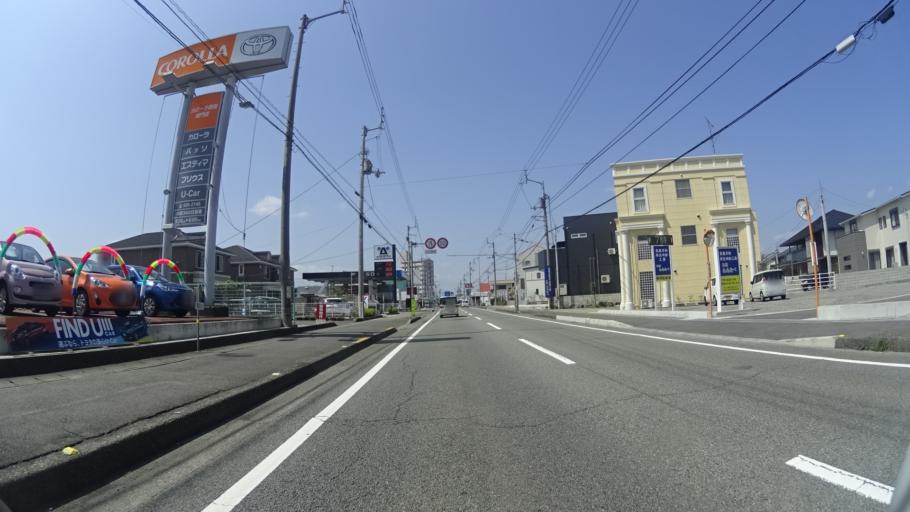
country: JP
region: Tokushima
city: Narutocho-mitsuishi
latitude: 34.1641
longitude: 134.5963
